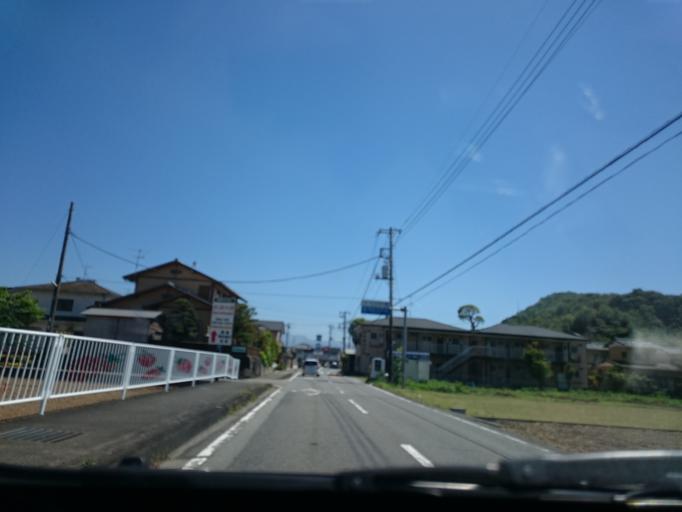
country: JP
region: Shizuoka
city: Mishima
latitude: 35.0570
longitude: 138.9318
